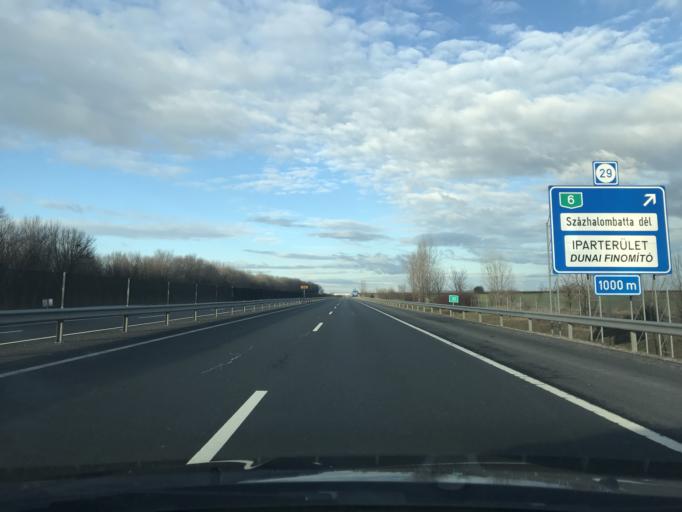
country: HU
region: Fejer
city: Rackeresztur
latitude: 47.2905
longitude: 18.8641
